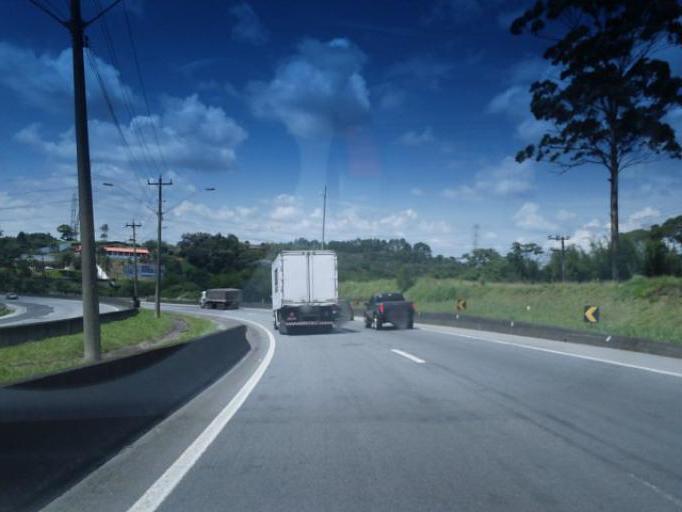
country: BR
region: Sao Paulo
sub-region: Sao Lourenco Da Serra
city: Sao Lourenco da Serra
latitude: -23.8069
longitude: -46.9241
